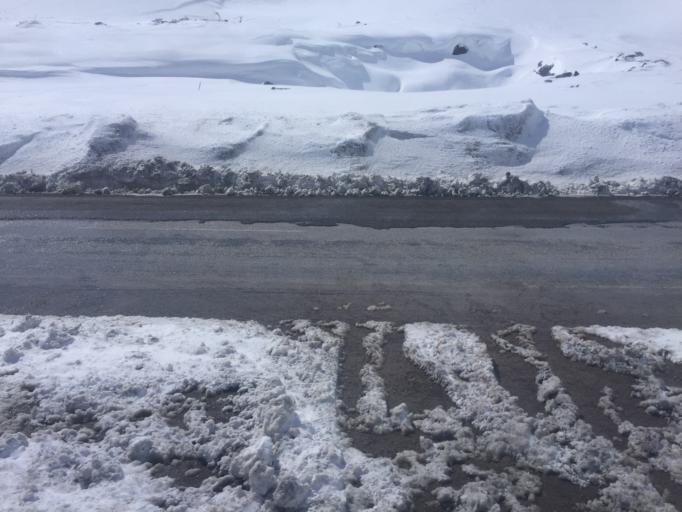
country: TR
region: Kahramanmaras
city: Goksun
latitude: 38.1992
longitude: 36.4540
